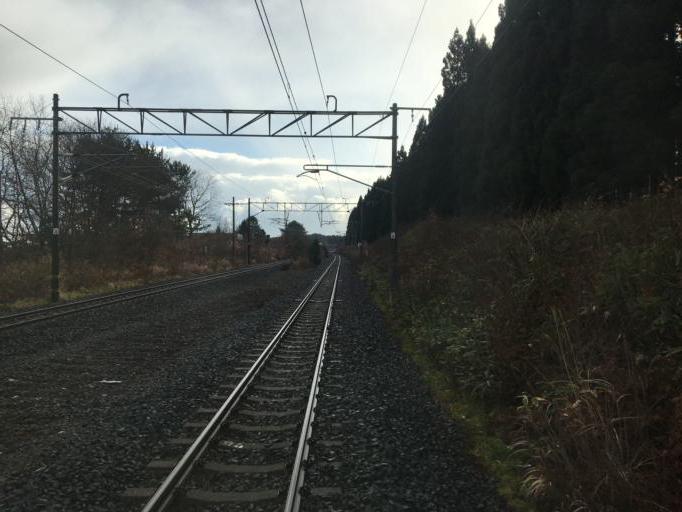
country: JP
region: Aomori
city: Aomori Shi
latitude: 40.9195
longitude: 141.0287
